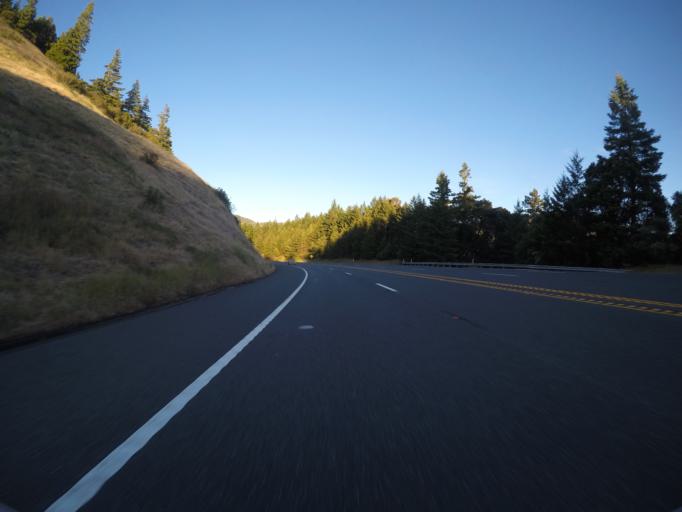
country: US
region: California
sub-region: Mendocino County
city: Laytonville
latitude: 39.8264
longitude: -123.6721
